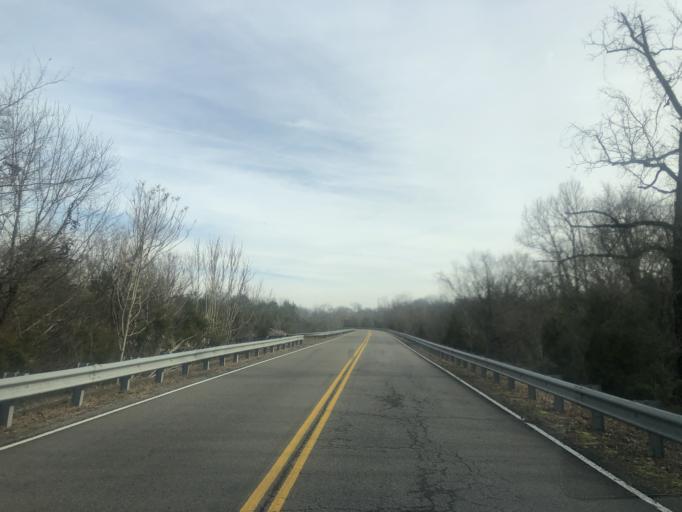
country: US
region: Tennessee
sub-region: Williamson County
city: Nolensville
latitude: 35.8578
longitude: -86.5764
